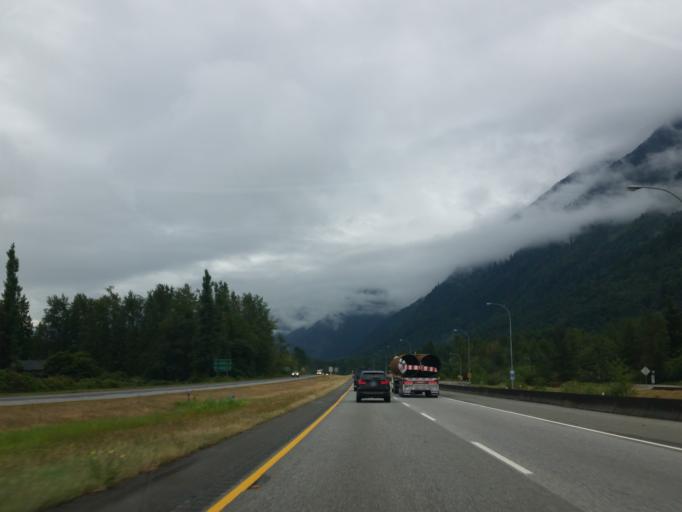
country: CA
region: British Columbia
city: Agassiz
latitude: 49.1832
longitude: -121.7557
